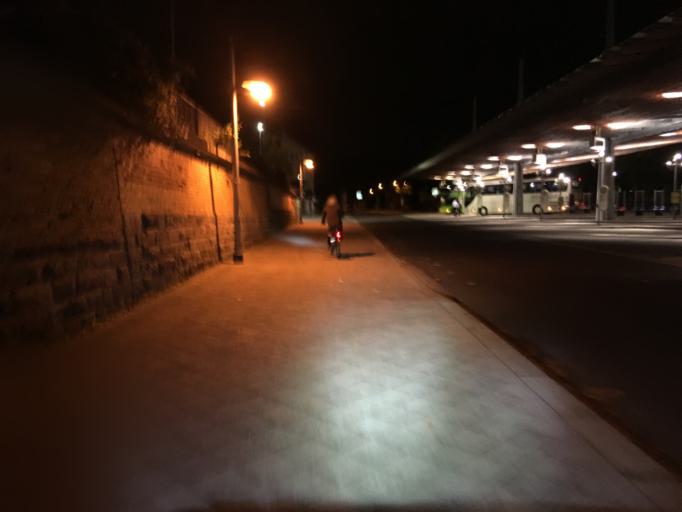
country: DE
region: Saxony-Anhalt
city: Magdeburg
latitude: 52.1316
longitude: 11.6249
